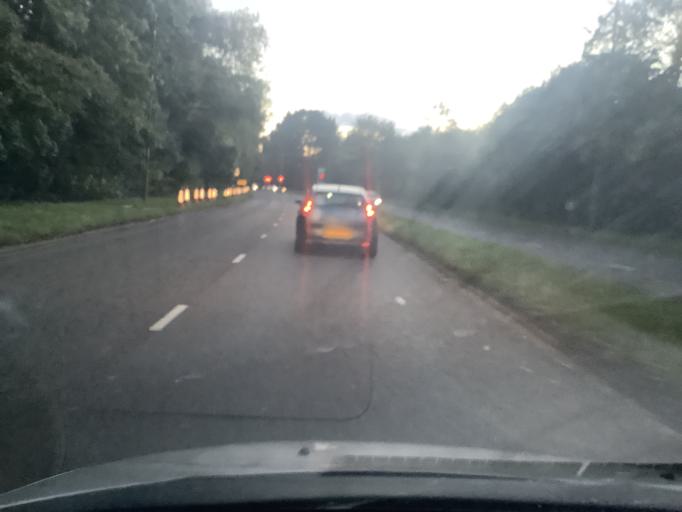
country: GB
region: England
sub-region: Hampshire
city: Marchwood
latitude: 50.9250
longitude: -1.4436
